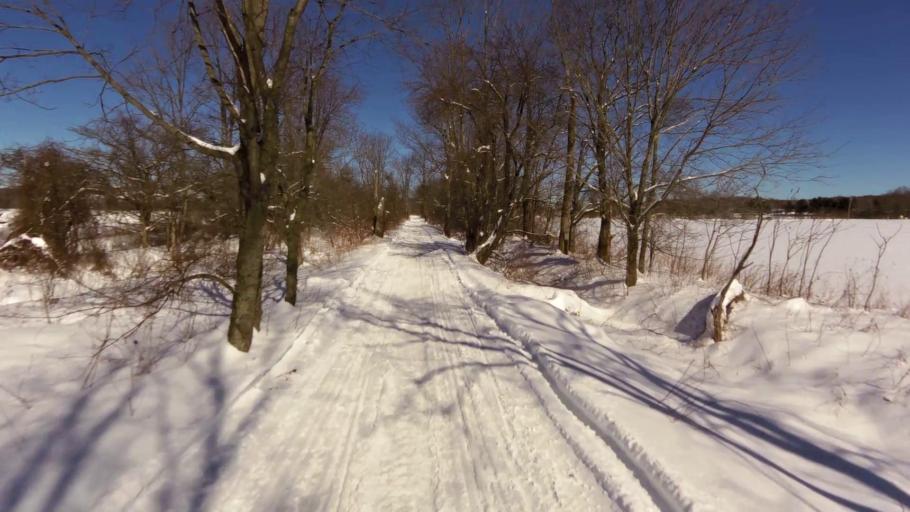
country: US
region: New York
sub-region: Chautauqua County
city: Celoron
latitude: 42.2441
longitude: -79.2684
